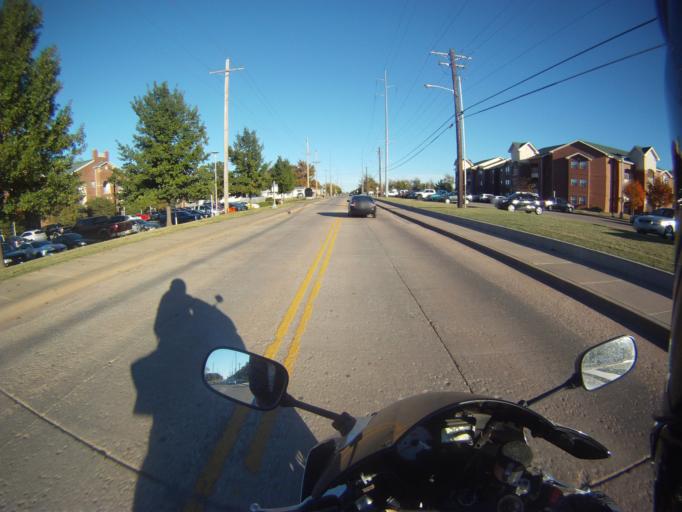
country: US
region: Oklahoma
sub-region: Payne County
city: Stillwater
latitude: 36.1305
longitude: -97.0740
